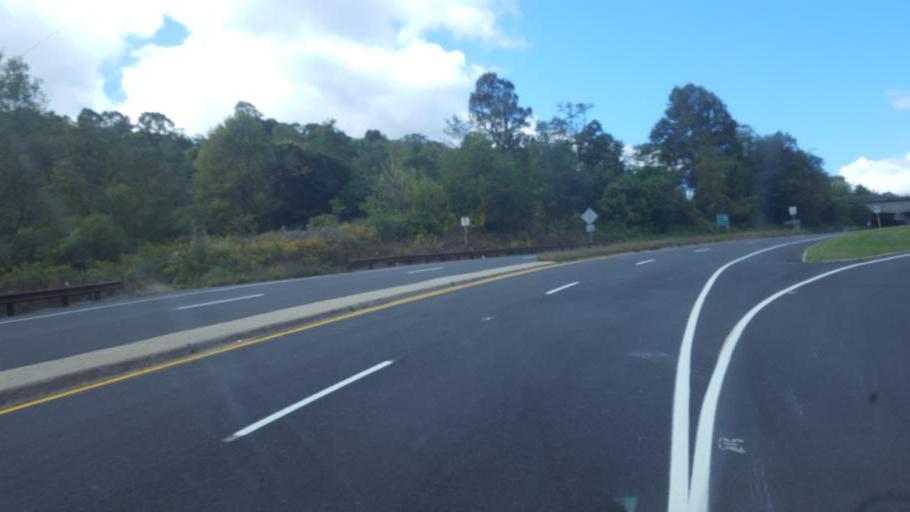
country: US
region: Virginia
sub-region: Page County
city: Luray
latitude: 38.6610
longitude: -78.3186
